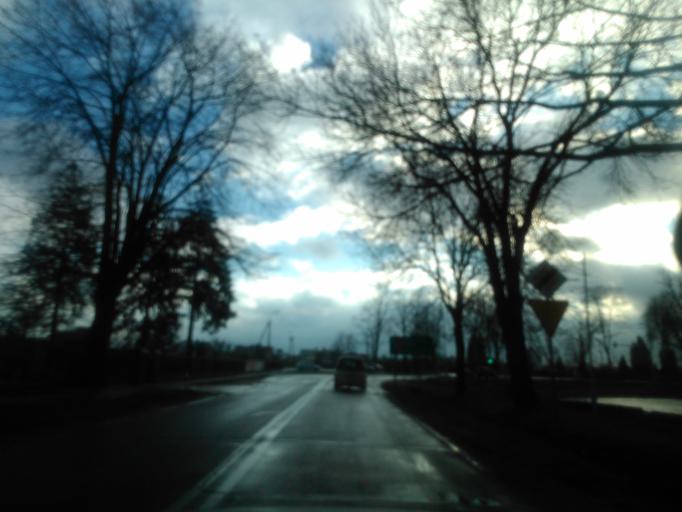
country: PL
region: Masovian Voivodeship
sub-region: Powiat sierpecki
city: Sierpc
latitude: 52.8649
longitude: 19.6644
